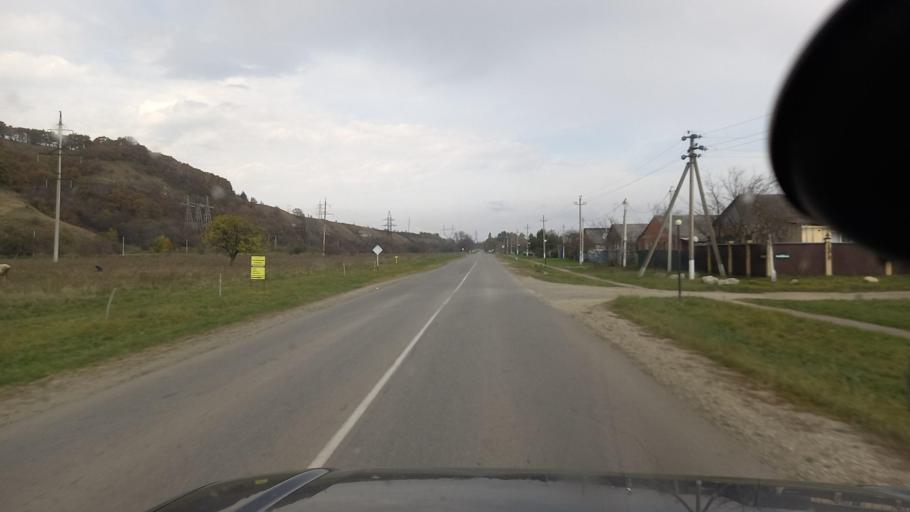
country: RU
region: Krasnodarskiy
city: Psebay
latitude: 44.1552
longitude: 40.8333
